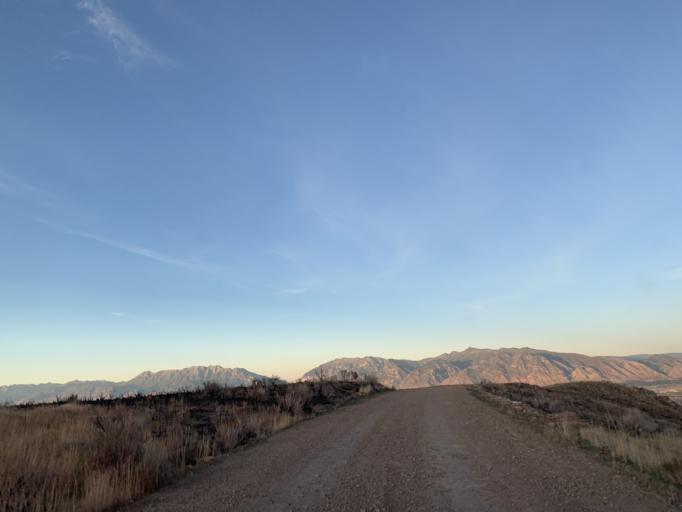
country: US
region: Utah
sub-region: Utah County
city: West Mountain
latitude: 40.0954
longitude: -111.8213
